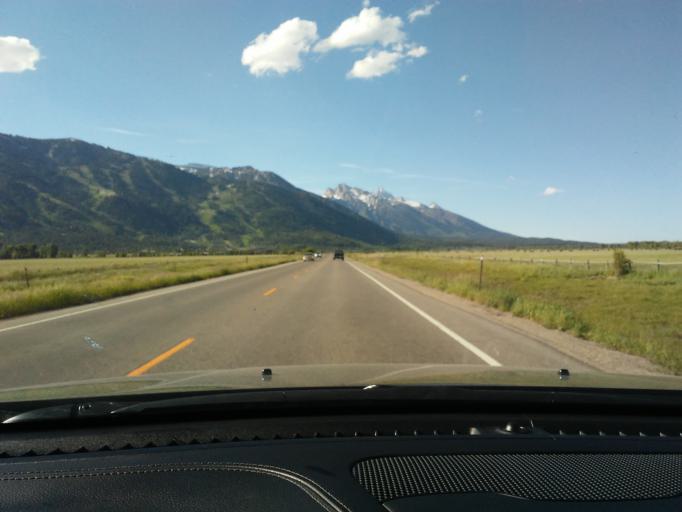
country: US
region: Wyoming
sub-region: Teton County
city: Moose Wilson Road
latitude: 43.5625
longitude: -110.8220
